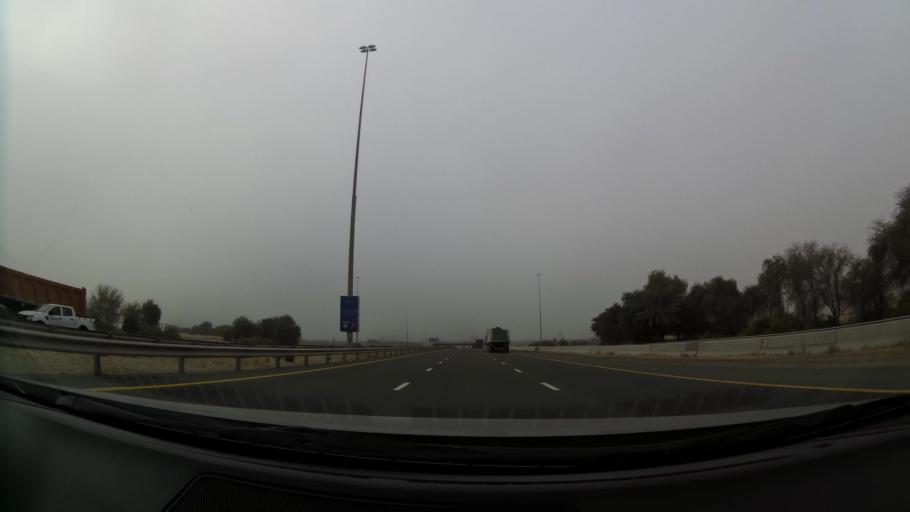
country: AE
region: Dubai
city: Dubai
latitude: 25.1237
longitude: 55.3617
